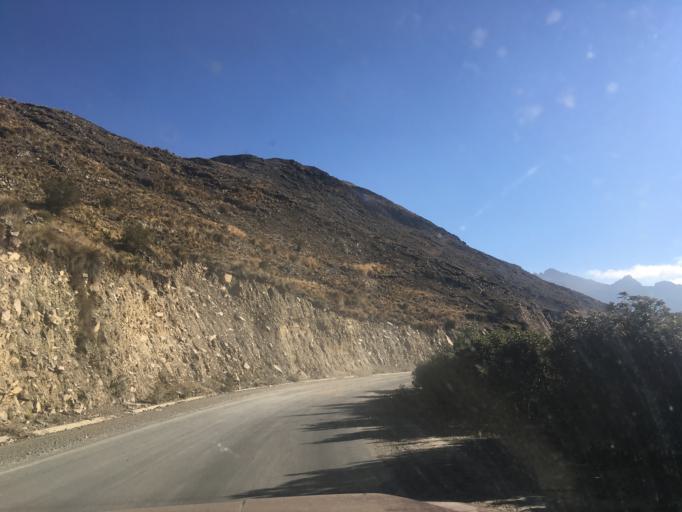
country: BO
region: La Paz
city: Quime
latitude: -17.0174
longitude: -67.2789
